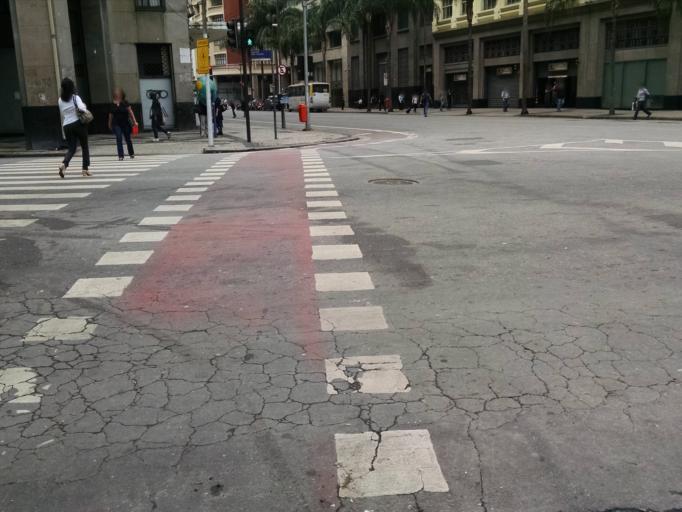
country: BR
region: Rio de Janeiro
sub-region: Rio De Janeiro
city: Rio de Janeiro
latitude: -22.9064
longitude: -43.1752
